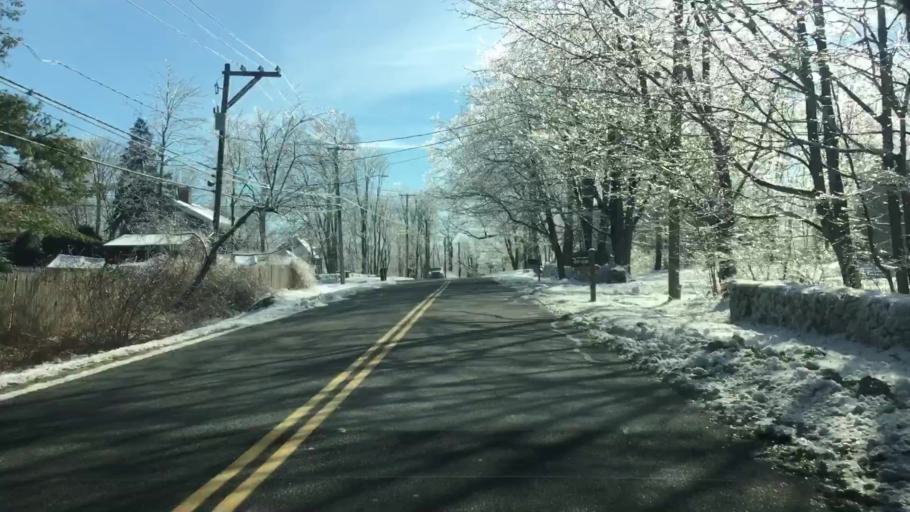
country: US
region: Connecticut
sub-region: Fairfield County
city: Trumbull
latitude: 41.3245
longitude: -73.2210
